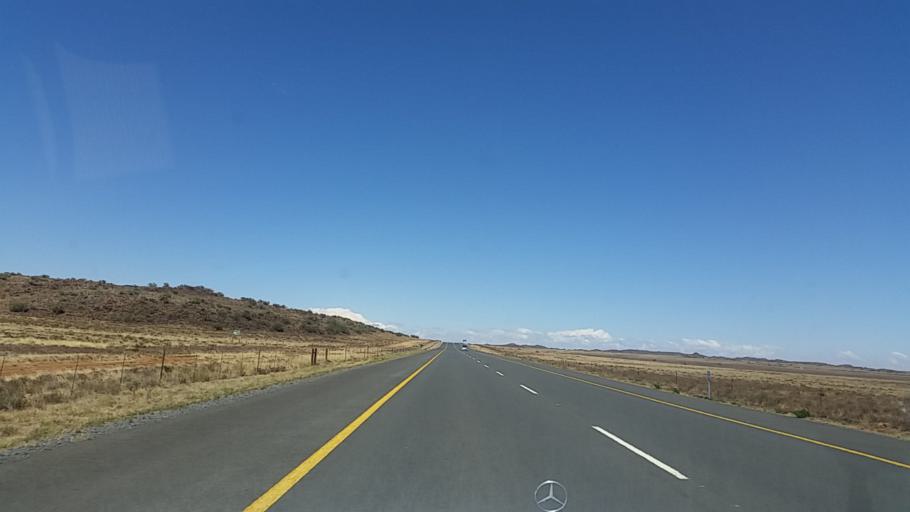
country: ZA
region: Northern Cape
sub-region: Pixley ka Seme District Municipality
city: Noupoort
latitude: -30.9778
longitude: 25.0138
